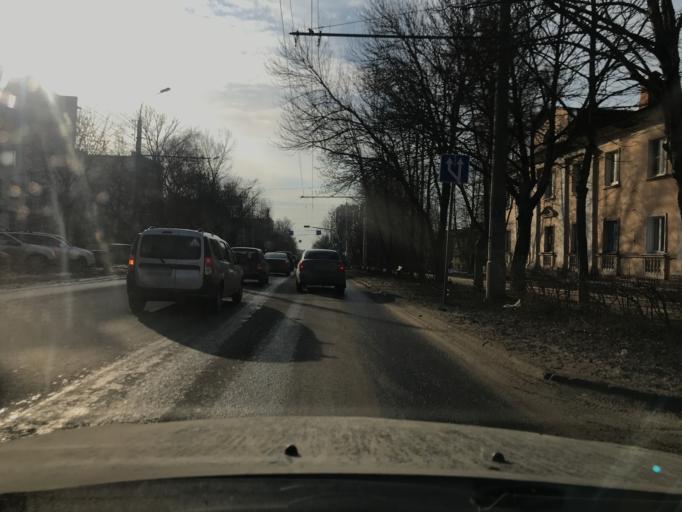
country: RU
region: Kaluga
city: Kaluga
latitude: 54.5215
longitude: 36.2557
